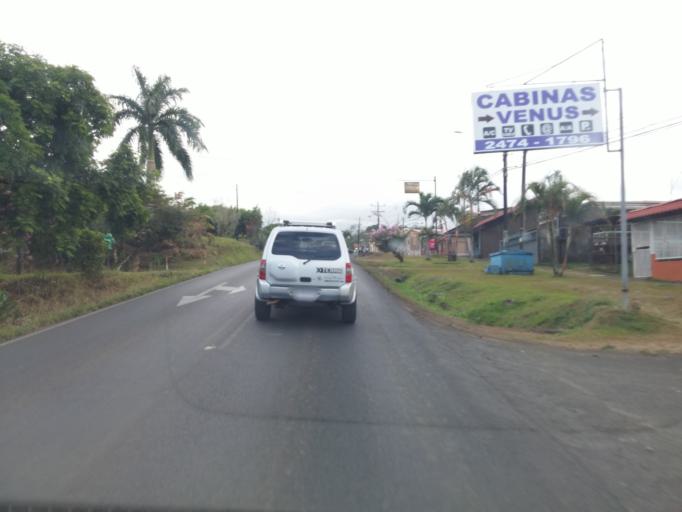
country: CR
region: Alajuela
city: Pital
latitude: 10.3889
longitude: -84.3391
